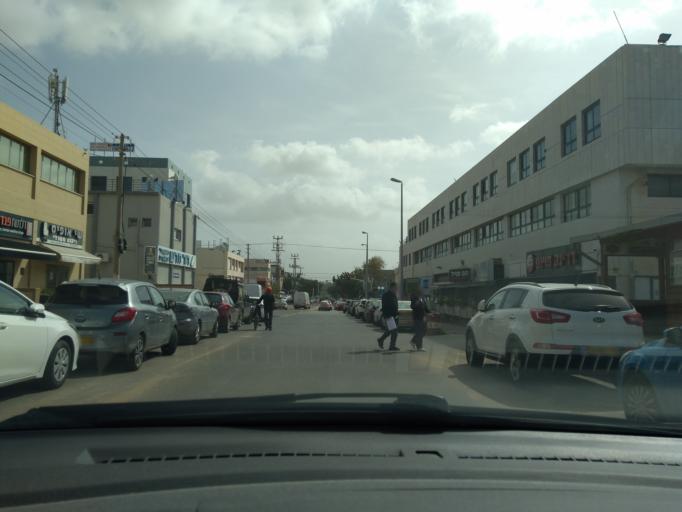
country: IL
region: Central District
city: Even Yehuda
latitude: 32.2807
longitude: 34.8597
